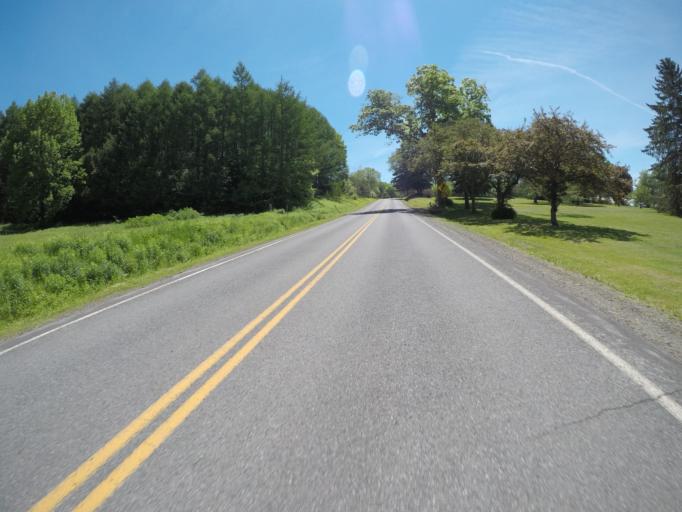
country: US
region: New York
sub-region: Delaware County
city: Delhi
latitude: 42.1892
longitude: -74.8045
